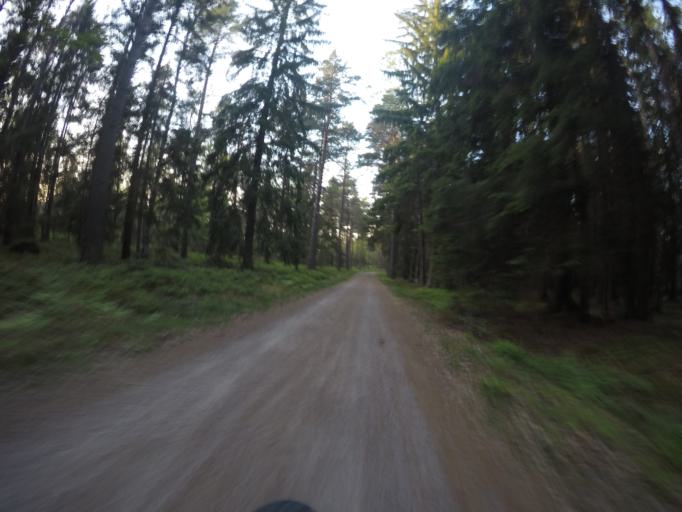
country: SE
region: Soedermanland
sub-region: Eskilstuna Kommun
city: Eskilstuna
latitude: 59.3439
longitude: 16.5106
